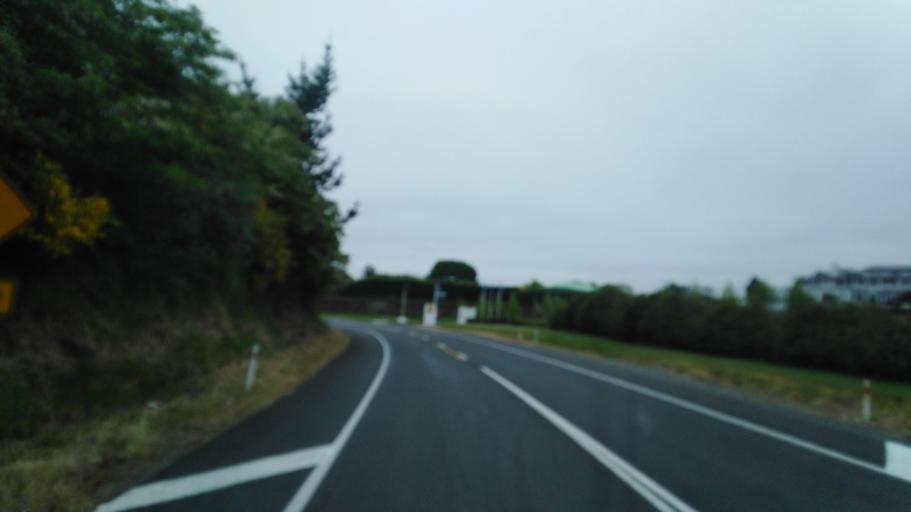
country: NZ
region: Waikato
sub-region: Taupo District
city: Taupo
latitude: -38.7046
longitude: 176.1006
